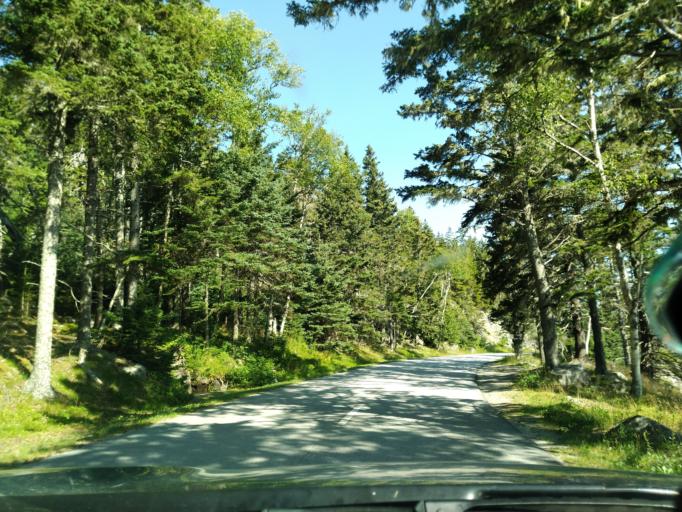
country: US
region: Maine
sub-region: Hancock County
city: Gouldsboro
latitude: 44.3457
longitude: -68.0457
